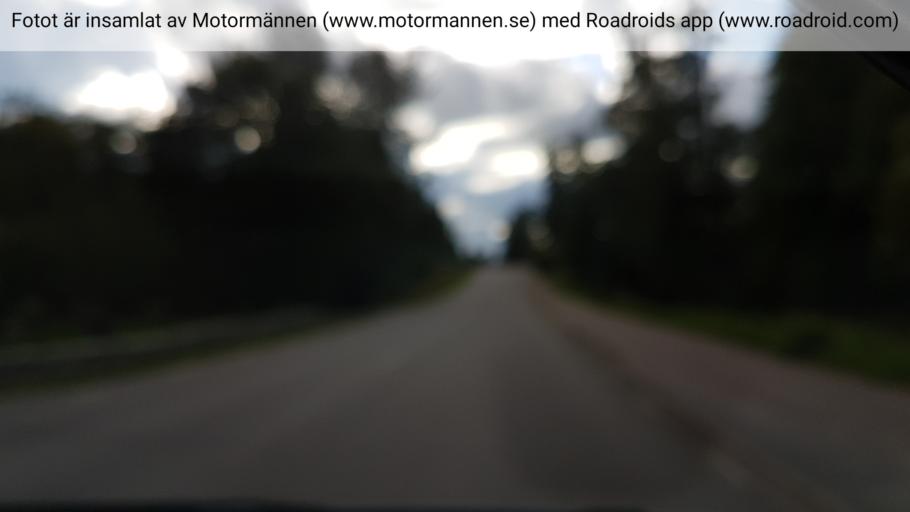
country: SE
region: Vaestra Goetaland
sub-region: Tibro Kommun
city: Tibro
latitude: 58.4154
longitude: 14.1842
